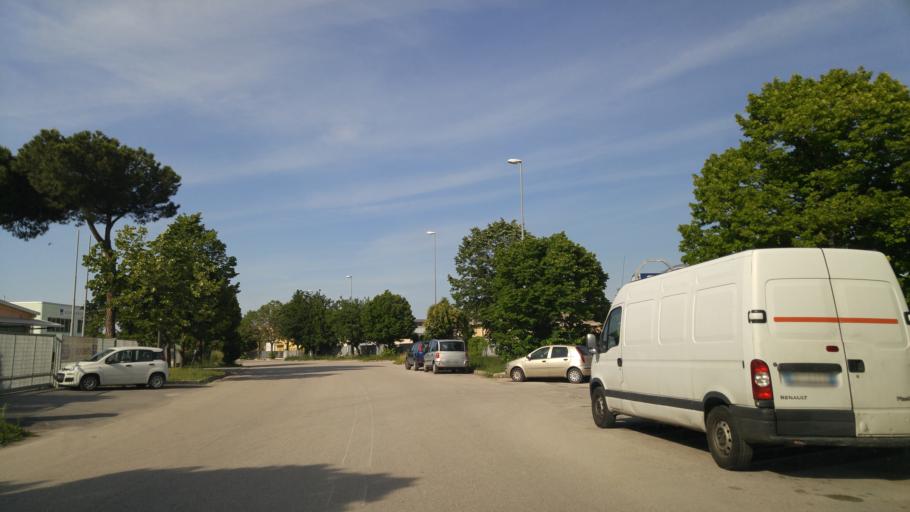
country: IT
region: The Marches
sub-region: Provincia di Pesaro e Urbino
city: Bellocchi
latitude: 43.7987
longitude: 13.0151
